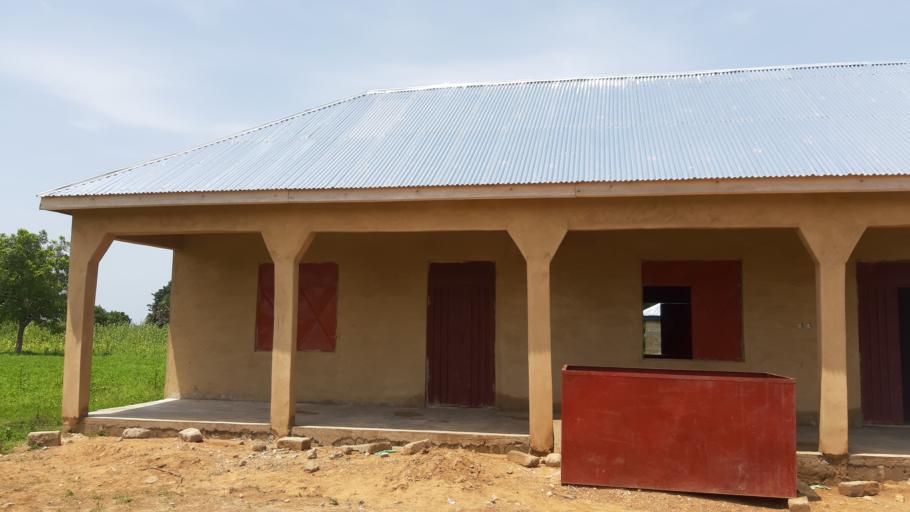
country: GH
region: Upper East
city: Bolgatanga
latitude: 10.7820
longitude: -0.7874
